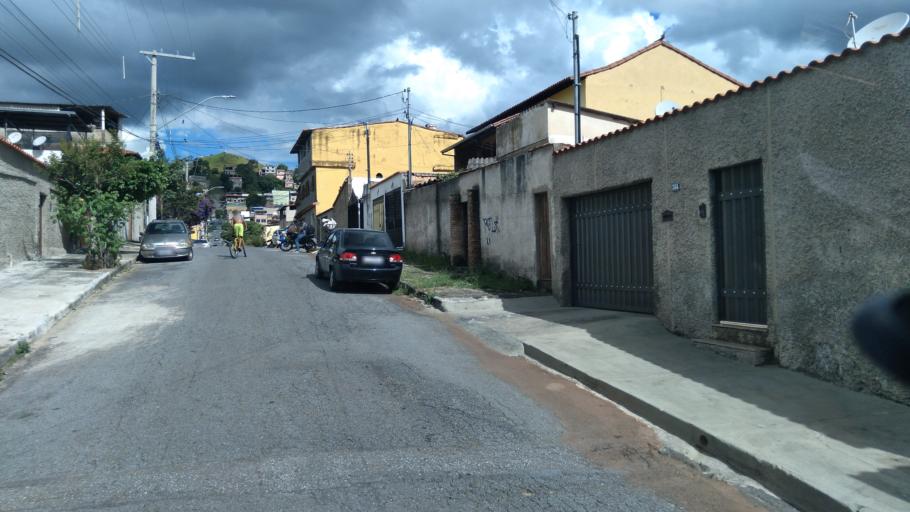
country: BR
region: Minas Gerais
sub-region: Belo Horizonte
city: Belo Horizonte
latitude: -19.8912
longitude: -43.8949
